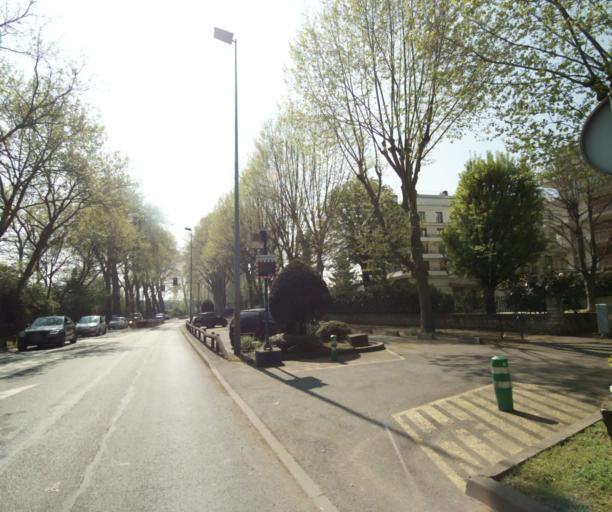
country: FR
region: Ile-de-France
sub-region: Departement des Hauts-de-Seine
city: Saint-Cloud
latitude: 48.8502
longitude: 2.2238
